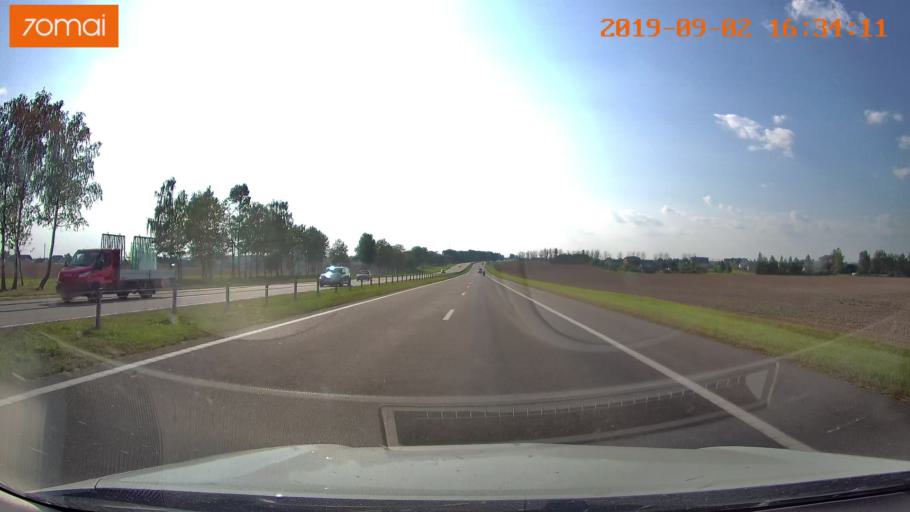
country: BY
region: Minsk
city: Smilavichy
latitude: 53.7592
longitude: 28.0439
